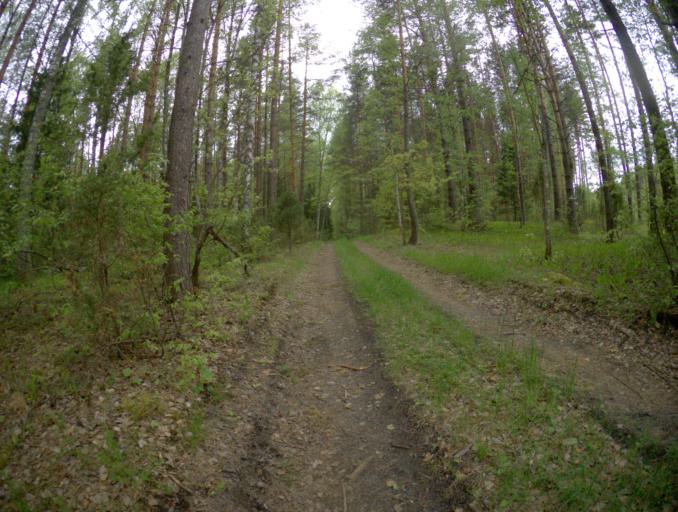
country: RU
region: Rjazan
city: Gus'-Zheleznyy
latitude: 55.1274
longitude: 41.1531
